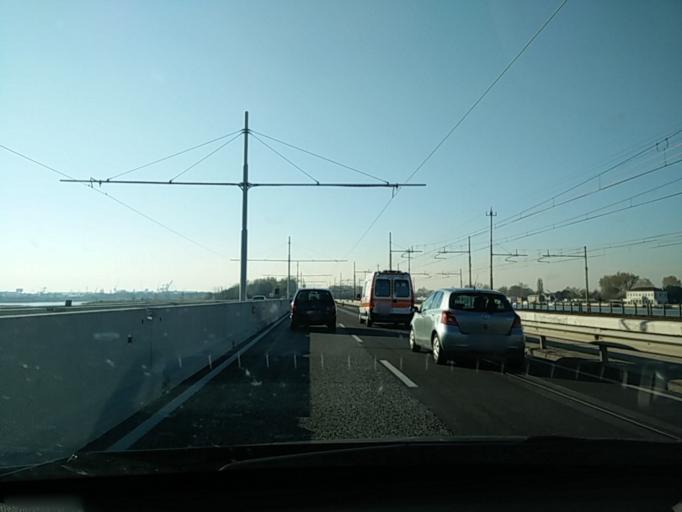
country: IT
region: Veneto
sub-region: Provincia di Venezia
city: Campalto
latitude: 45.4622
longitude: 12.2838
